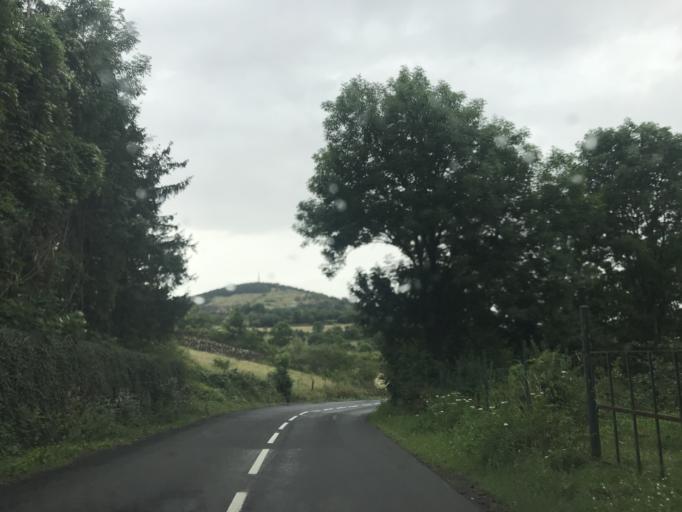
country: FR
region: Auvergne
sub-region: Departement de la Haute-Loire
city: Espaly-Saint-Marcel
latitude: 45.0600
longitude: 3.8734
